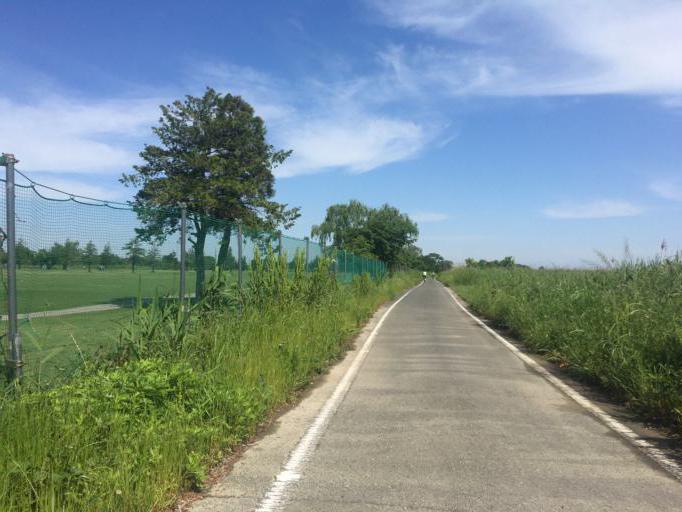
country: JP
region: Saitama
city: Shiki
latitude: 35.8671
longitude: 139.5818
